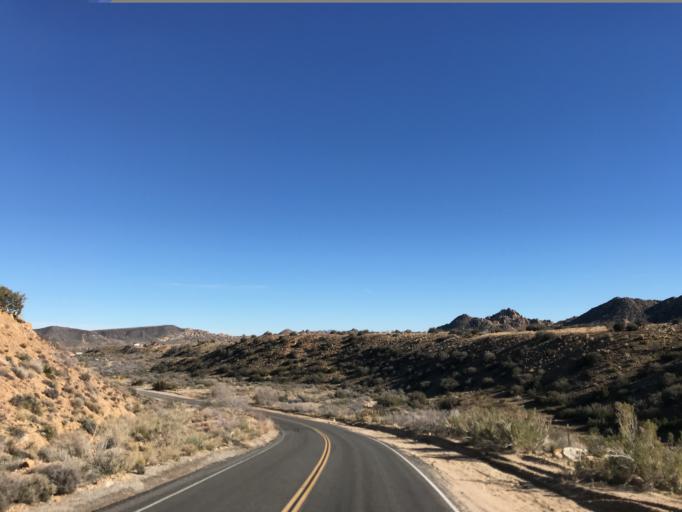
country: US
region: California
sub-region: San Bernardino County
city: Yucca Valley
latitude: 34.1618
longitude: -116.5131
